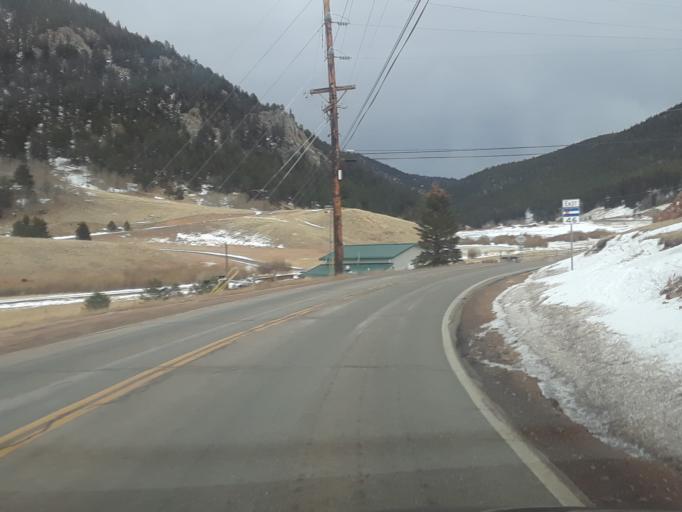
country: US
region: Colorado
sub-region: Gilpin County
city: Central City
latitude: 39.8368
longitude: -105.4348
